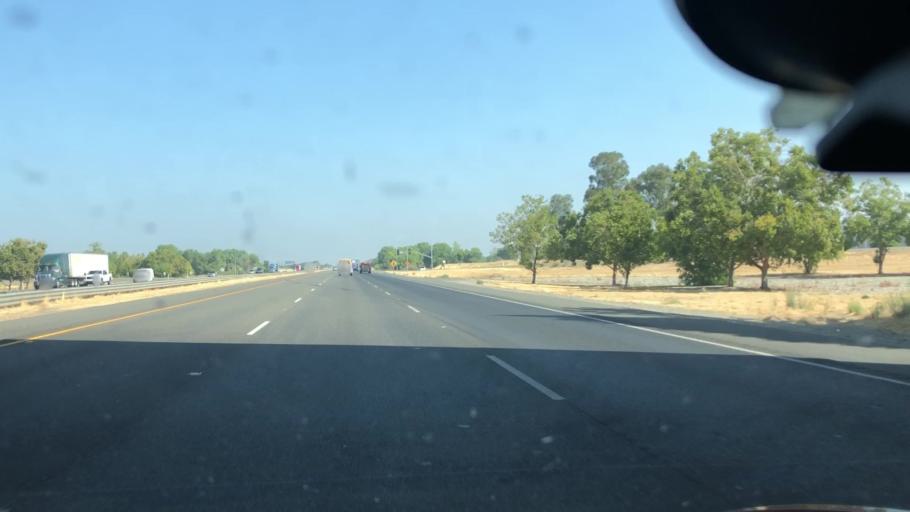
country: US
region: California
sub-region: Sacramento County
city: Laguna
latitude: 38.4262
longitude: -121.4872
